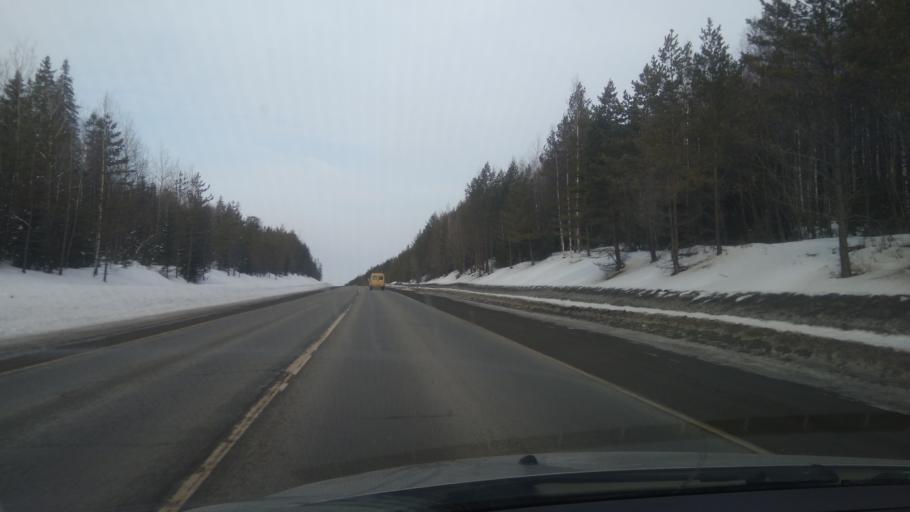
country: RU
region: Sverdlovsk
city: Atig
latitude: 56.8232
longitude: 59.3246
